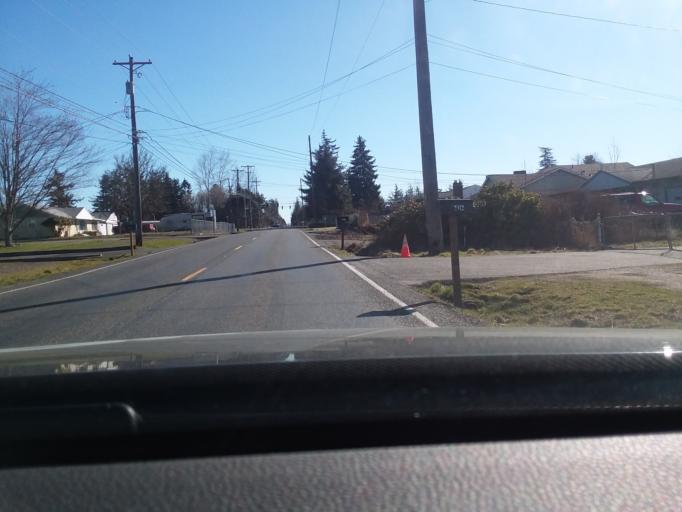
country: US
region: Washington
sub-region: Pierce County
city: Midland
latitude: 47.1622
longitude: -122.3911
